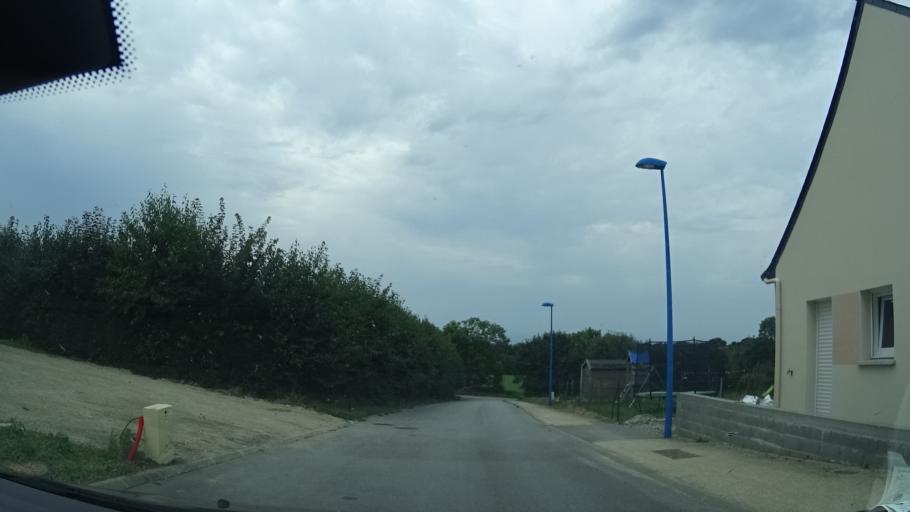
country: FR
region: Brittany
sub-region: Departement du Finistere
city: Plouarzel
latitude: 48.4359
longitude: -4.7324
